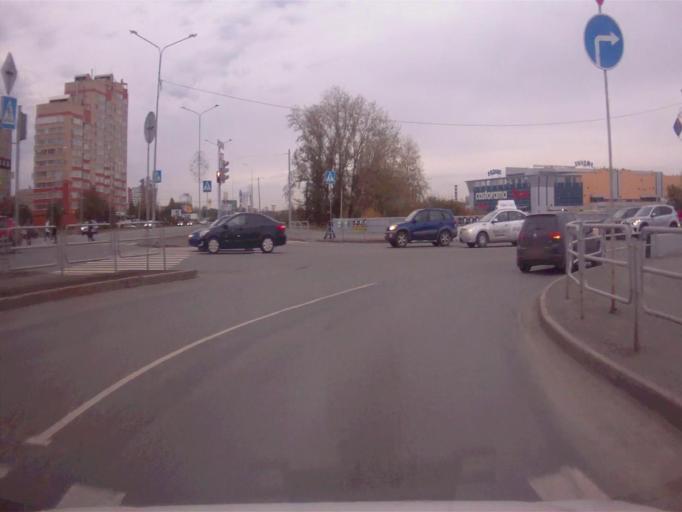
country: RU
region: Chelyabinsk
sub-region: Gorod Chelyabinsk
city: Chelyabinsk
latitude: 55.1742
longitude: 61.3478
